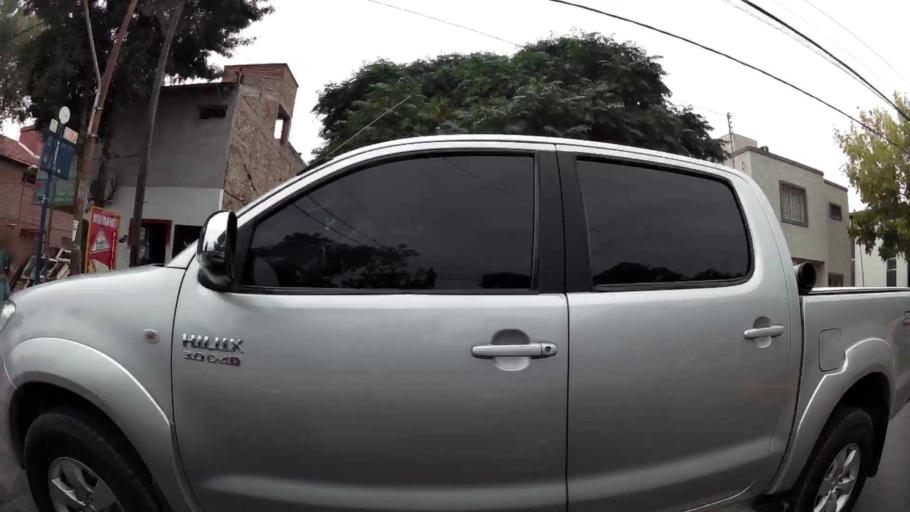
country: AR
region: Mendoza
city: Las Heras
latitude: -32.8657
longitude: -68.8549
